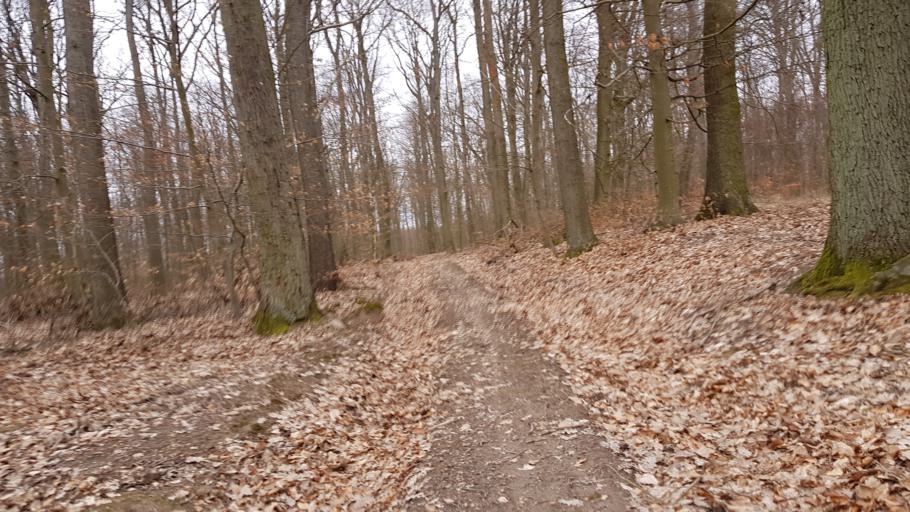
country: PL
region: West Pomeranian Voivodeship
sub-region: Powiat pyrzycki
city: Kozielice
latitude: 53.0806
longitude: 14.7476
